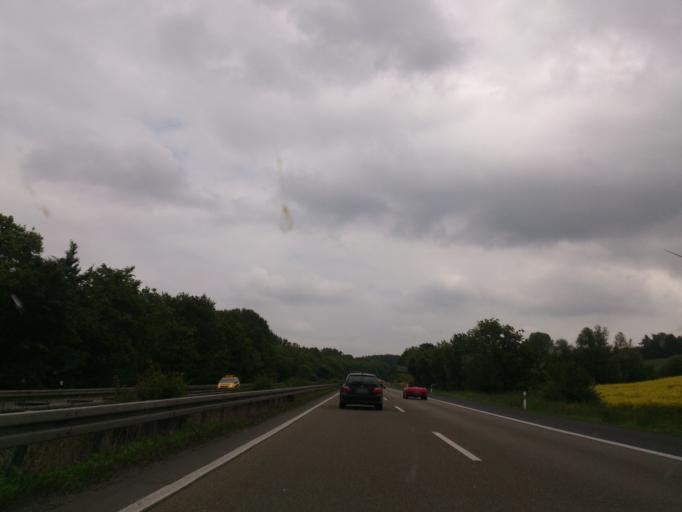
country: DE
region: Hesse
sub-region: Regierungsbezirk Kassel
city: Martinhagen
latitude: 51.3048
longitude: 9.3126
